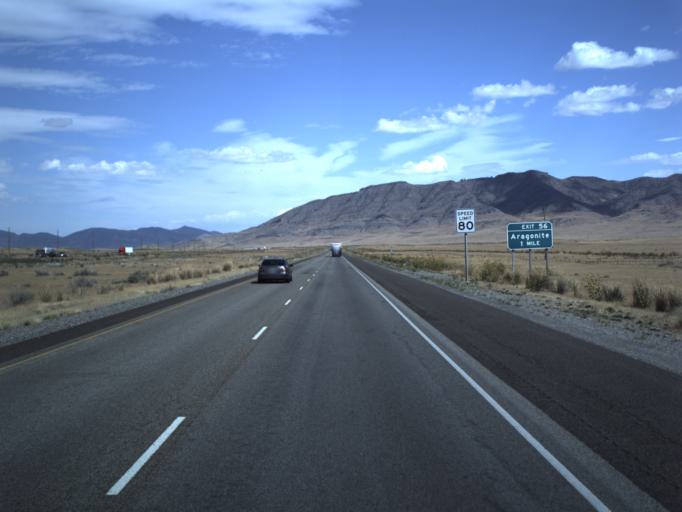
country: US
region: Utah
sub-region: Tooele County
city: Grantsville
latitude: 40.7609
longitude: -113.0064
